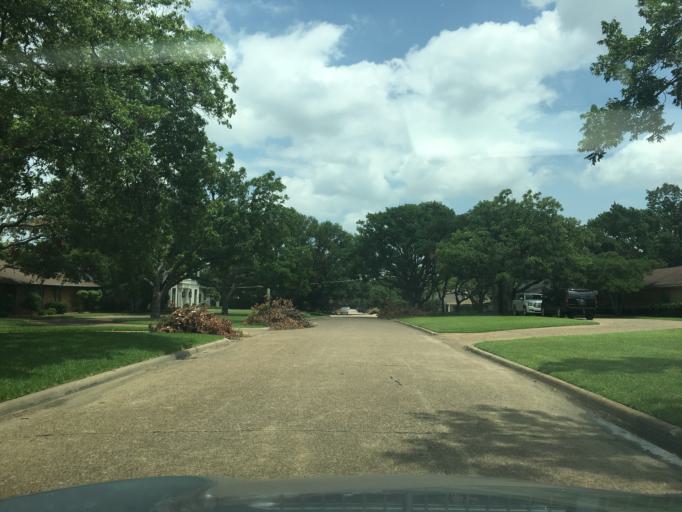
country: US
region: Texas
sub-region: Dallas County
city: University Park
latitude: 32.8963
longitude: -96.8309
